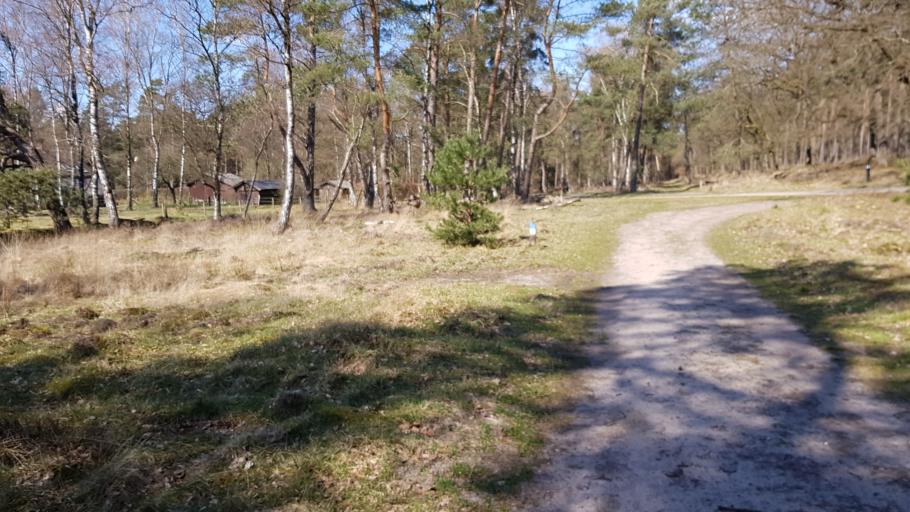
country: NL
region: Gelderland
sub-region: Gemeente Apeldoorn
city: Loenen
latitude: 52.0640
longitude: 6.0061
